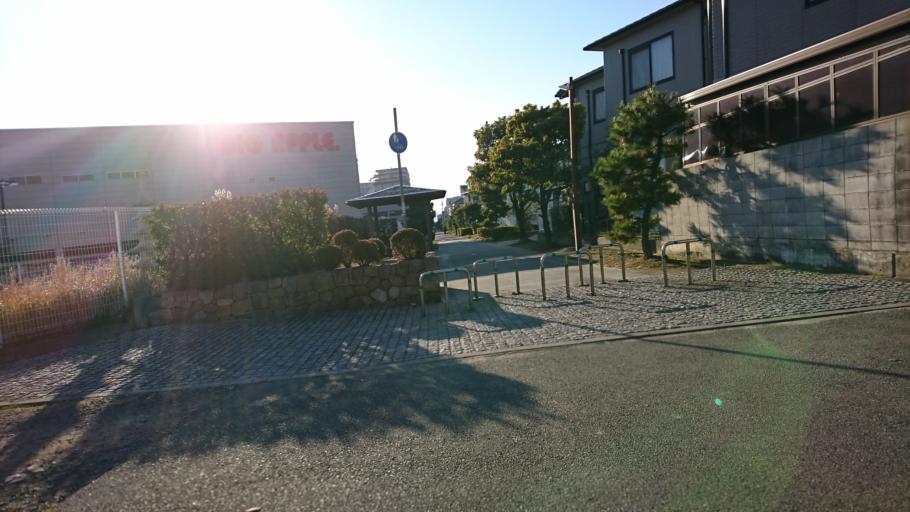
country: JP
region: Hyogo
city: Kakogawacho-honmachi
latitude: 34.7370
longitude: 134.8480
